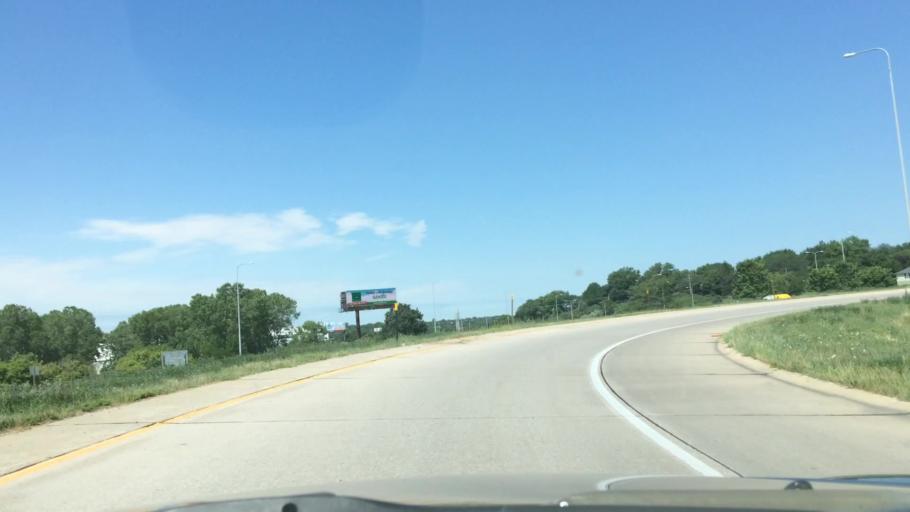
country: US
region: Nebraska
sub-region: Douglas County
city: Ralston
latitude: 41.2226
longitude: -96.0249
